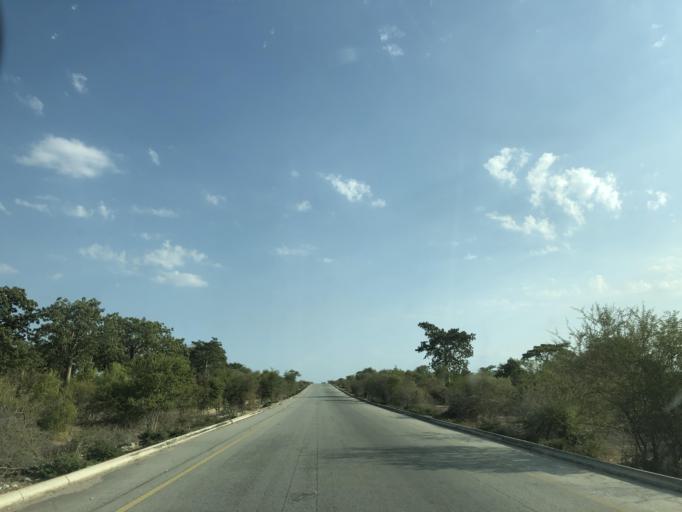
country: AO
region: Benguela
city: Benguela
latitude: -13.2031
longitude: 13.7635
